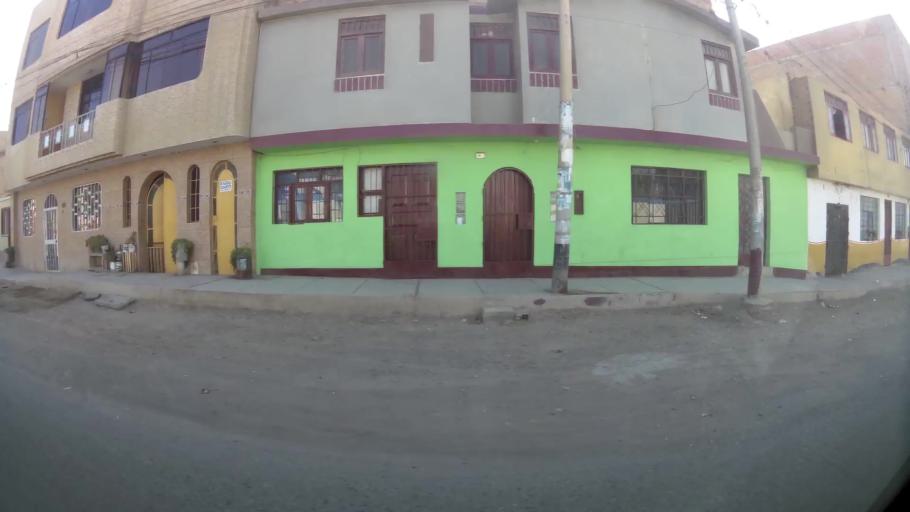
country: PE
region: Lima
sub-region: Huaura
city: Huacho
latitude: -11.1253
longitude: -77.6103
